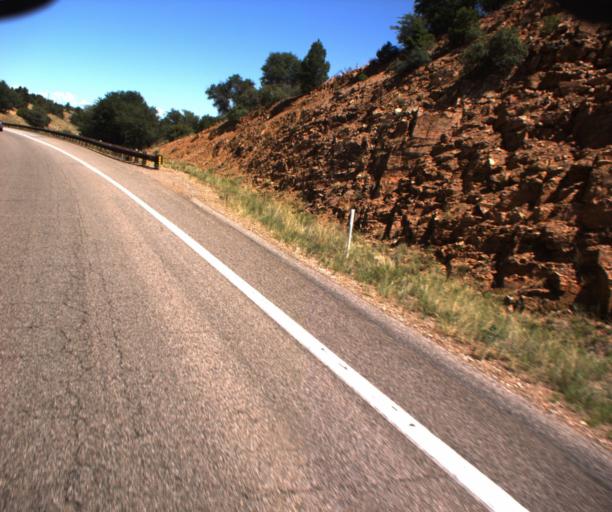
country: US
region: Arizona
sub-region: Gila County
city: Globe
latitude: 33.5117
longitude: -110.7005
